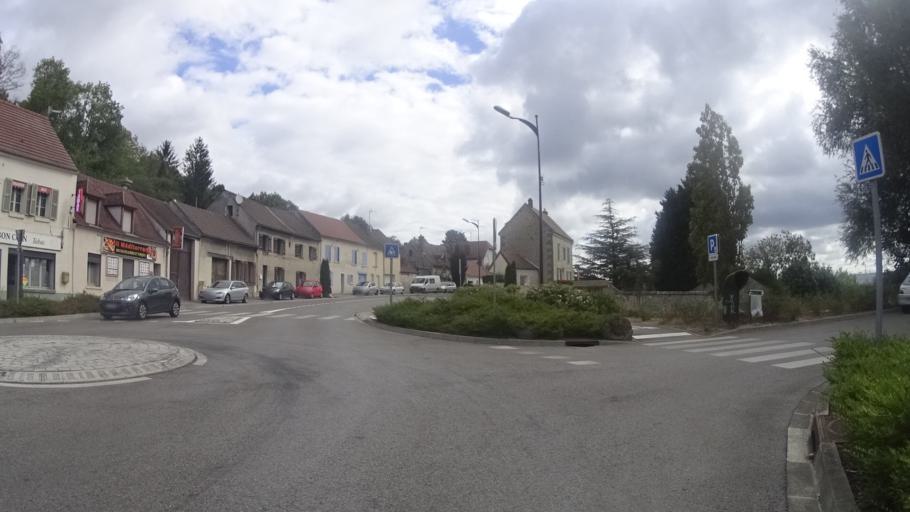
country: FR
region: Picardie
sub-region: Departement de l'Oise
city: Clairoix
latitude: 49.4402
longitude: 2.8529
